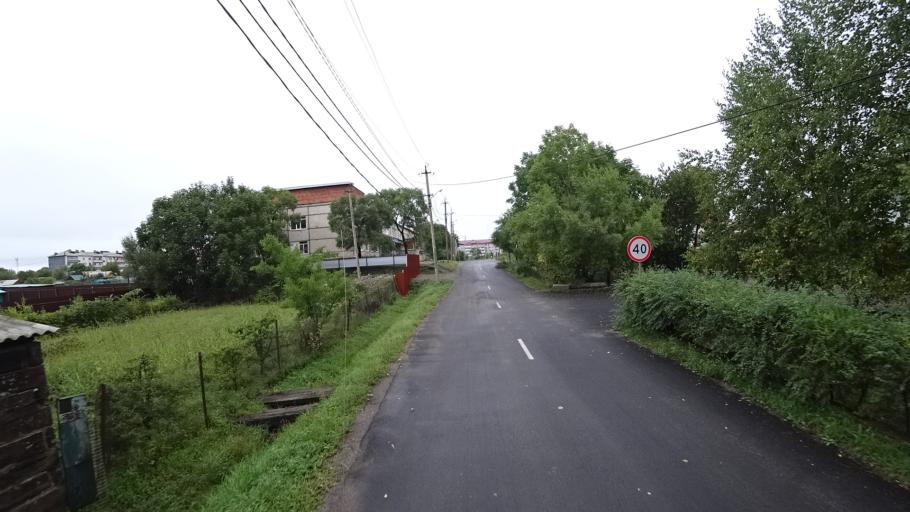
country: RU
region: Primorskiy
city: Monastyrishche
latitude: 44.2012
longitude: 132.4463
